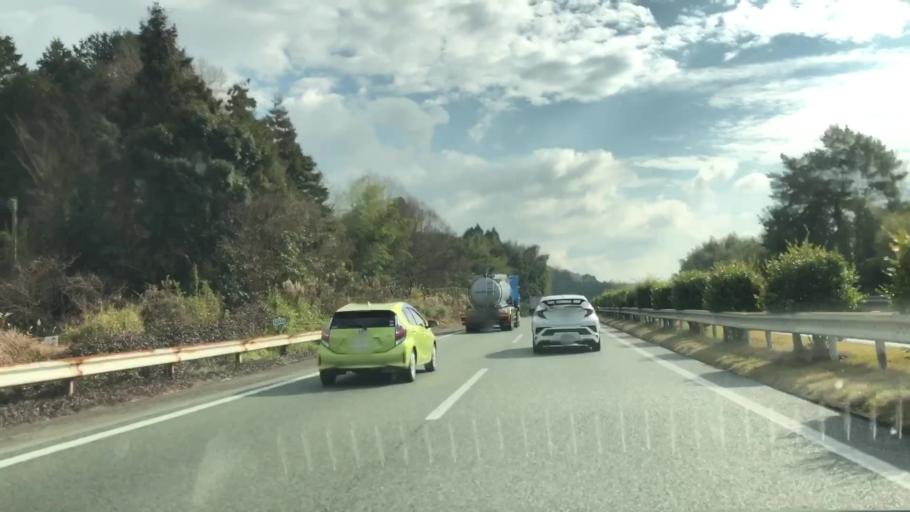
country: JP
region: Fukuoka
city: Setakamachi-takayanagi
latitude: 33.1100
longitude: 130.5324
